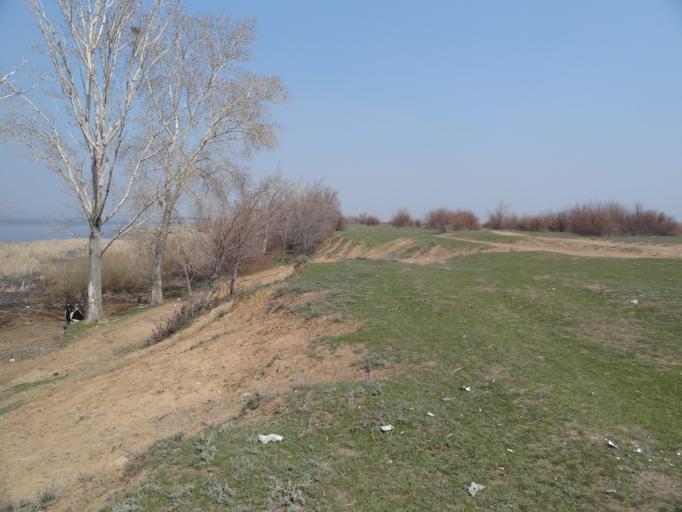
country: RU
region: Saratov
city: Privolzhskiy
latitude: 51.2703
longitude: 45.9293
